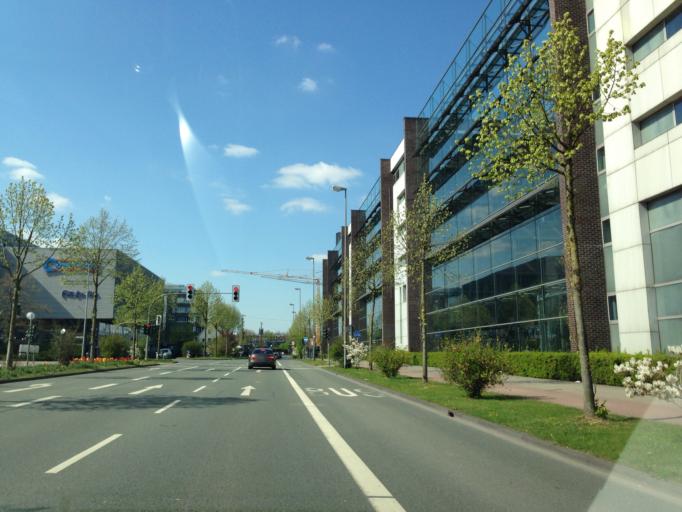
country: DE
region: North Rhine-Westphalia
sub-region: Regierungsbezirk Munster
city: Muenster
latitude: 51.9494
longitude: 7.6390
